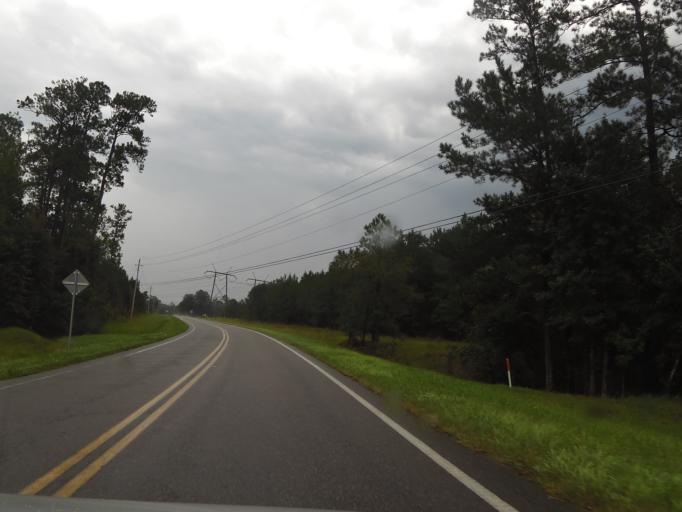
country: US
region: Florida
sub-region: Clay County
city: Middleburg
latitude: 30.0885
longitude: -81.8425
